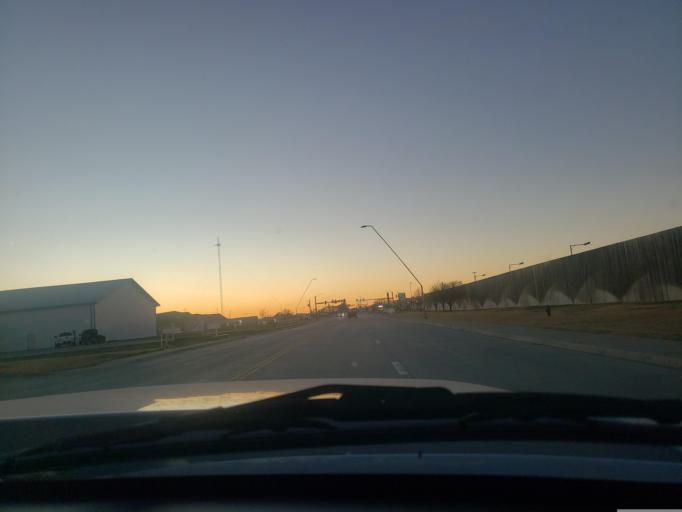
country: US
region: Kansas
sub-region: Finney County
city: Garden City
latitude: 37.9748
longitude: -100.8340
